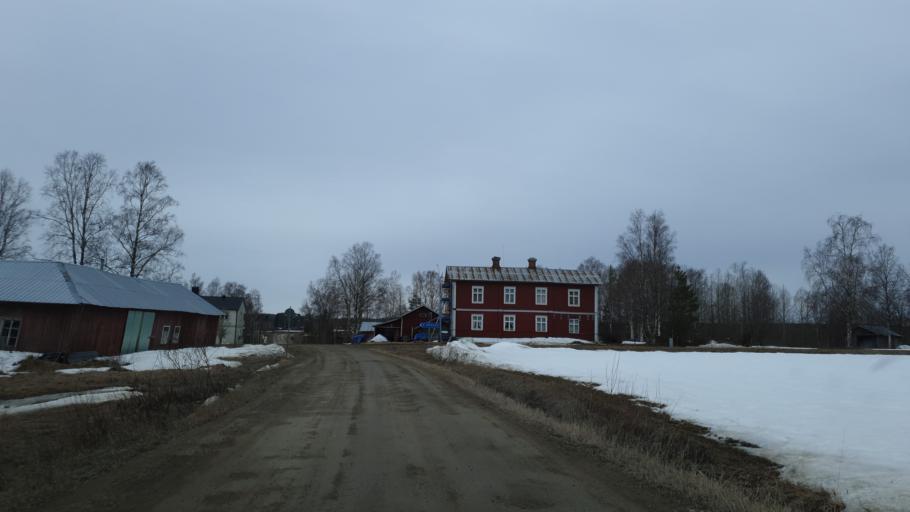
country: SE
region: Vaesterbotten
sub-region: Robertsfors Kommun
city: Robertsfors
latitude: 64.3825
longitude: 20.9202
